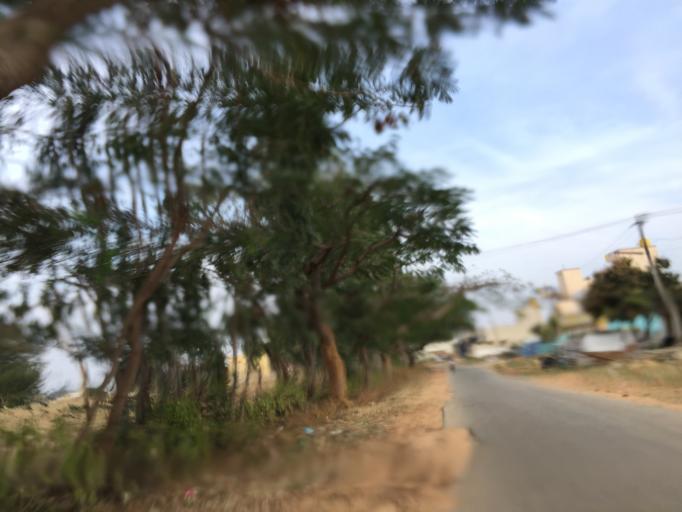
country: IN
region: Karnataka
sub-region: Kolar
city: Kolar
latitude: 13.1378
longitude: 78.1110
